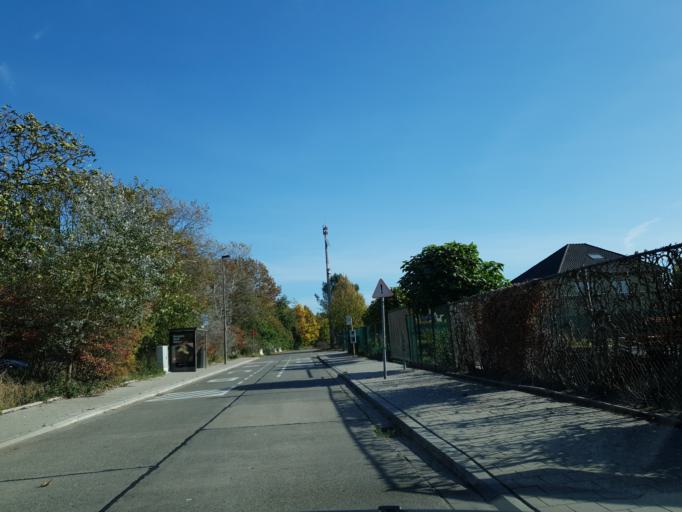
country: BE
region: Flanders
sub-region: Provincie Antwerpen
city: Stabroek
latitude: 51.3580
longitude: 4.3317
